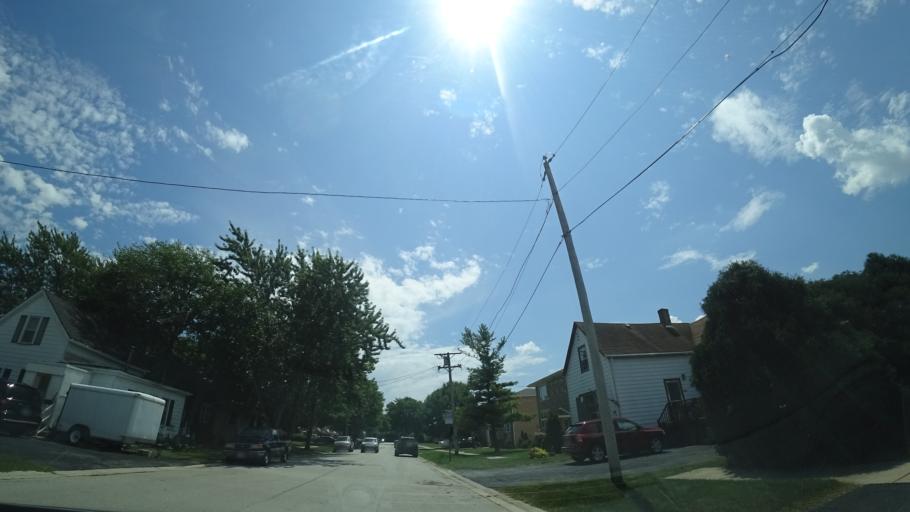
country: US
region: Illinois
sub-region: Cook County
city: Alsip
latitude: 41.6712
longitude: -87.7365
